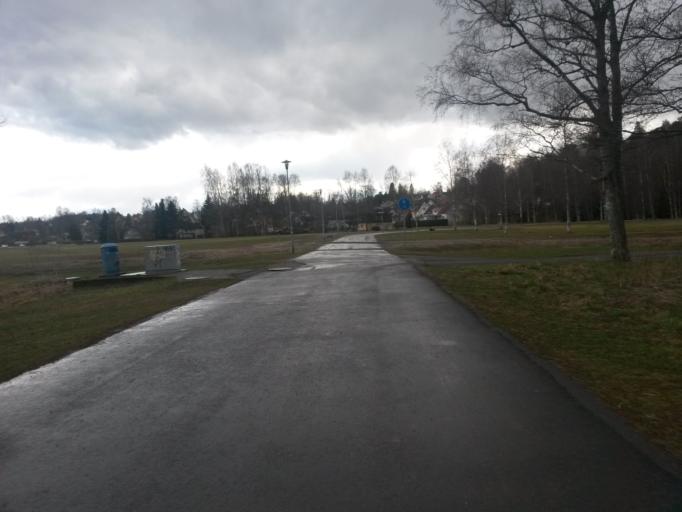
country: SE
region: OErebro
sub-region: Karlskoga Kommun
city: Karlskoga
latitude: 59.3161
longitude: 14.5145
